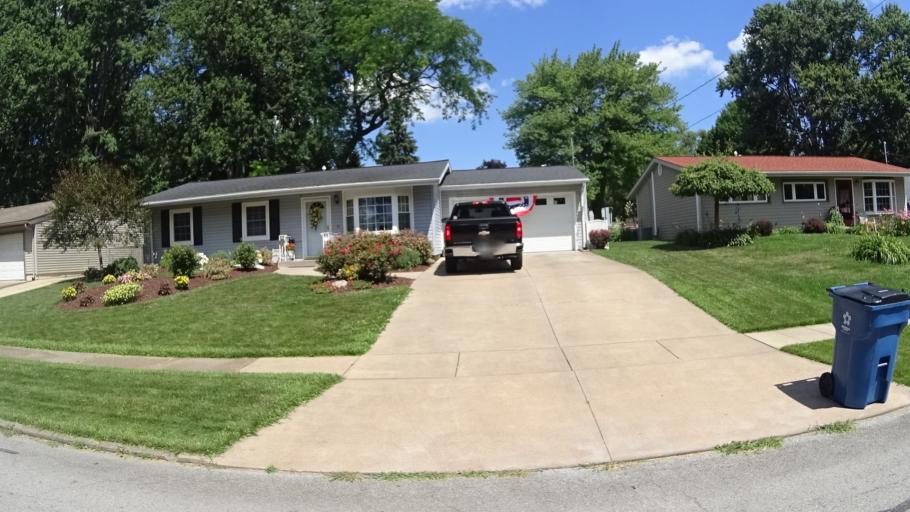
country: US
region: Ohio
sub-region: Erie County
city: Huron
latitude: 41.3876
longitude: -82.5629
